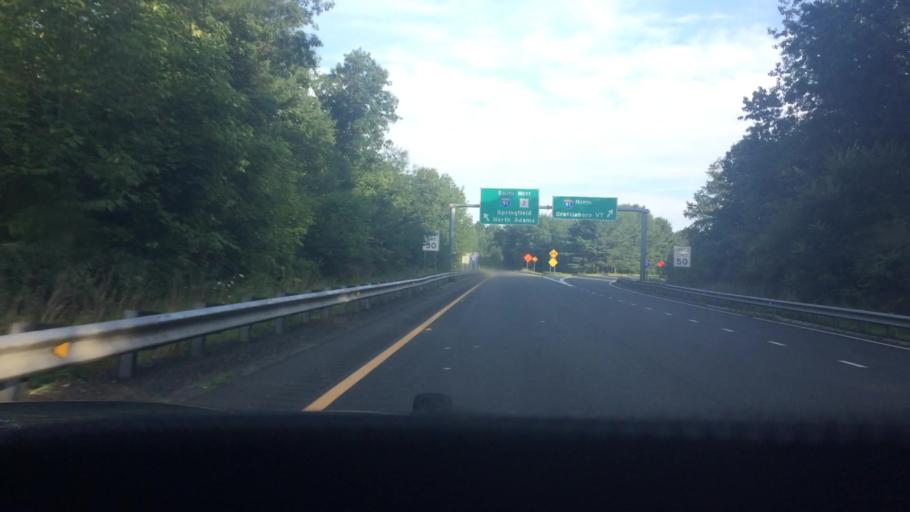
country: US
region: Massachusetts
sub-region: Franklin County
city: Greenfield
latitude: 42.6135
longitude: -72.5887
